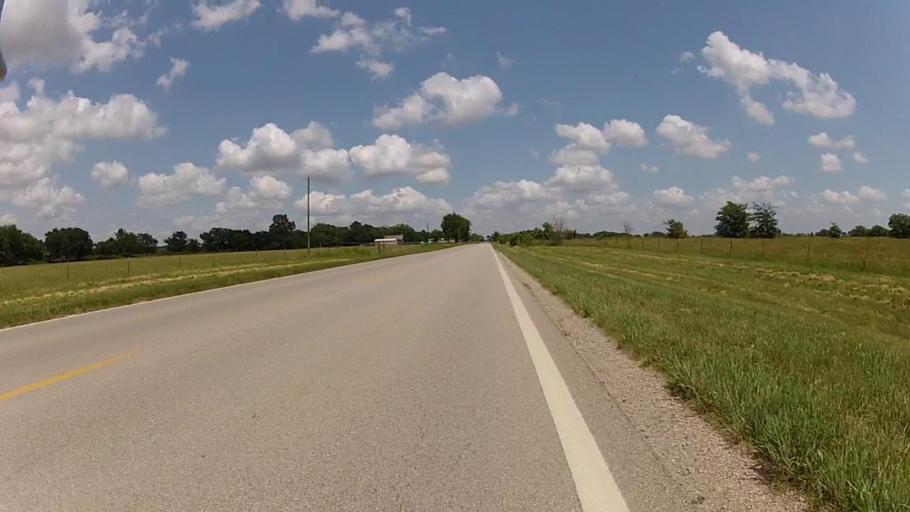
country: US
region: Kansas
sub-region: Labette County
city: Altamont
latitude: 37.1932
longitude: -95.3201
